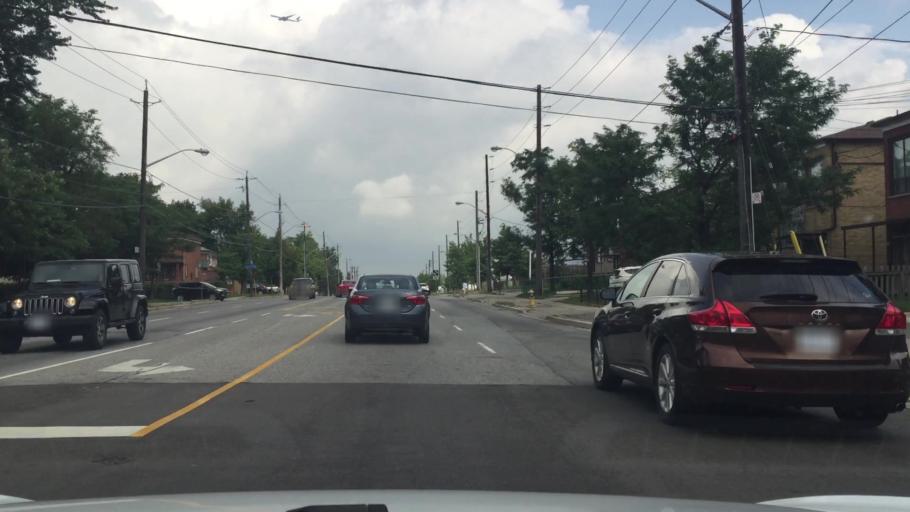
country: CA
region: Ontario
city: Concord
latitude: 43.7337
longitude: -79.4837
